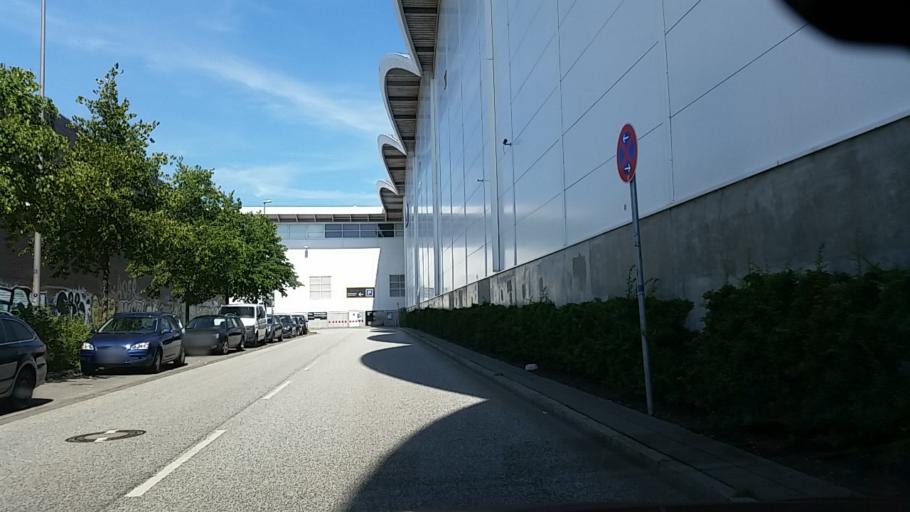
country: DE
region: Hamburg
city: St. Pauli
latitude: 53.5616
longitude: 9.9727
